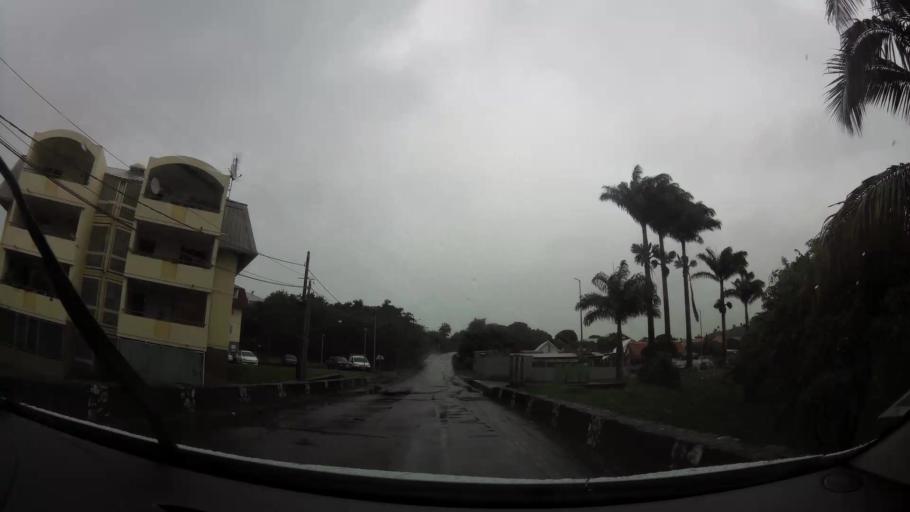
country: RE
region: Reunion
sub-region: Reunion
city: Saint-Andre
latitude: -20.9633
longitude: 55.6459
